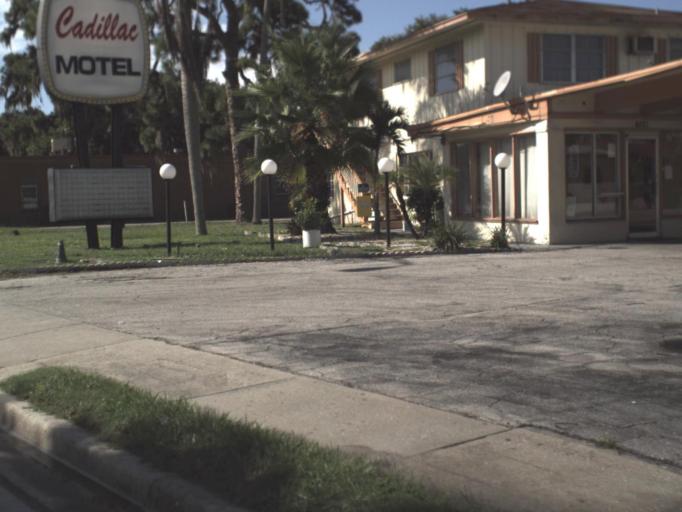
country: US
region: Florida
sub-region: Sarasota County
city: North Sarasota
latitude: 27.3700
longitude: -82.5527
